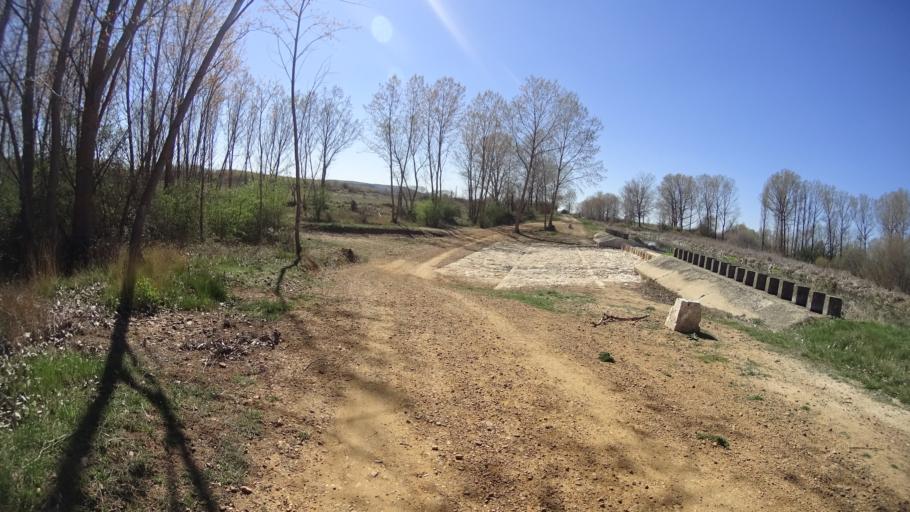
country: ES
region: Castille and Leon
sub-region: Provincia de Palencia
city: Osornillo
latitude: 42.4090
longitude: -4.2884
